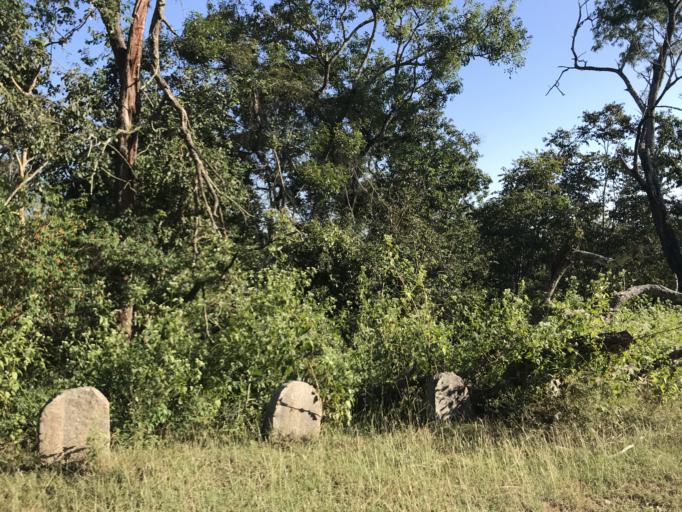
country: IN
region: Karnataka
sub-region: Mysore
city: Heggadadevankote
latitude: 11.9680
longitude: 76.2446
